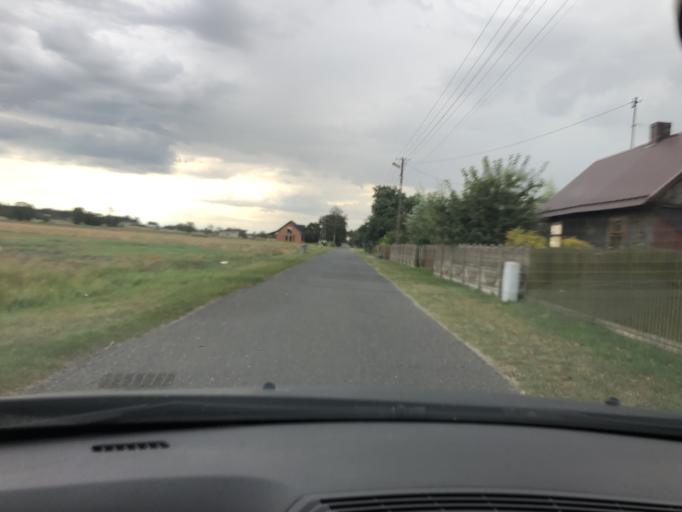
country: PL
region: Lodz Voivodeship
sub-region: Powiat wieruszowski
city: Czastary
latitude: 51.2407
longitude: 18.2894
